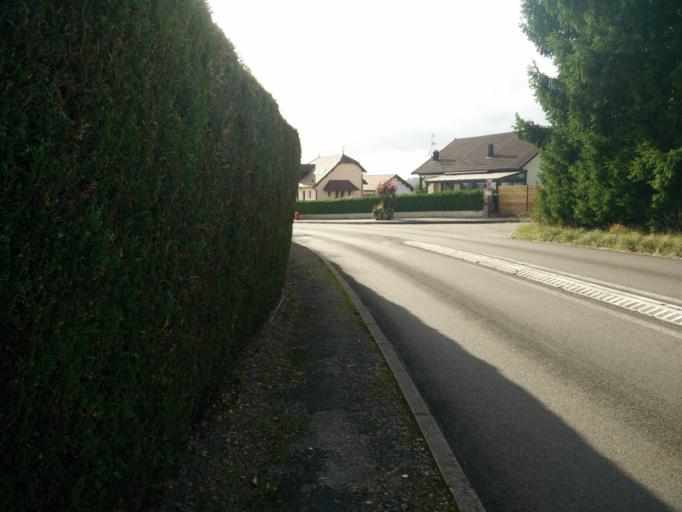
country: FR
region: Franche-Comte
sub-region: Departement du Doubs
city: Saone
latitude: 47.2270
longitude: 6.1248
